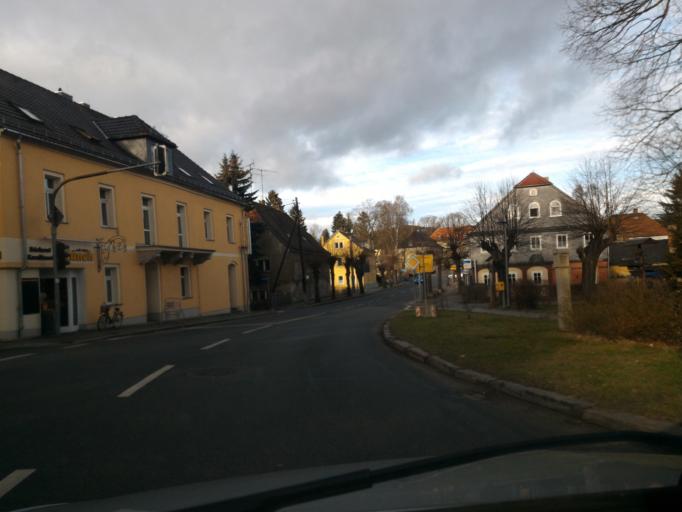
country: DE
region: Saxony
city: Oppach
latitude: 51.0584
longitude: 14.5029
